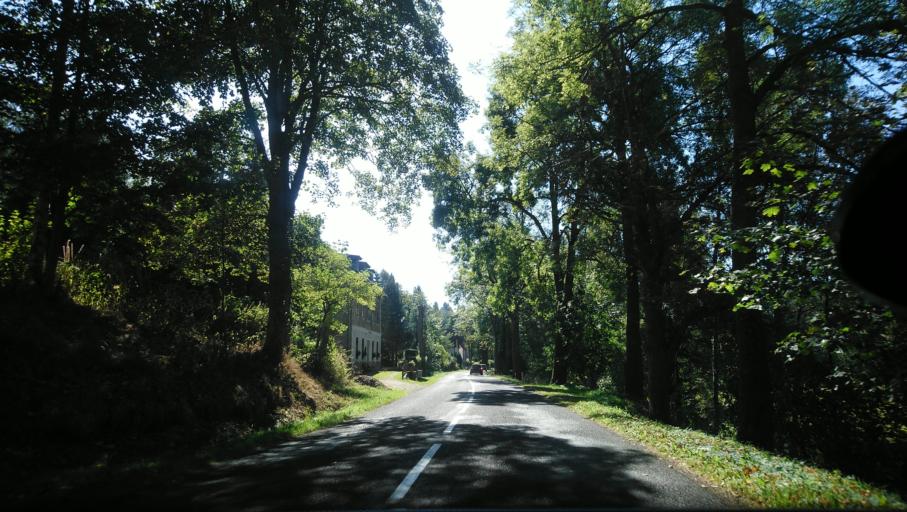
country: CZ
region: Ustecky
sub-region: Okres Chomutov
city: Vejprty
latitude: 50.4741
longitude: 13.0211
